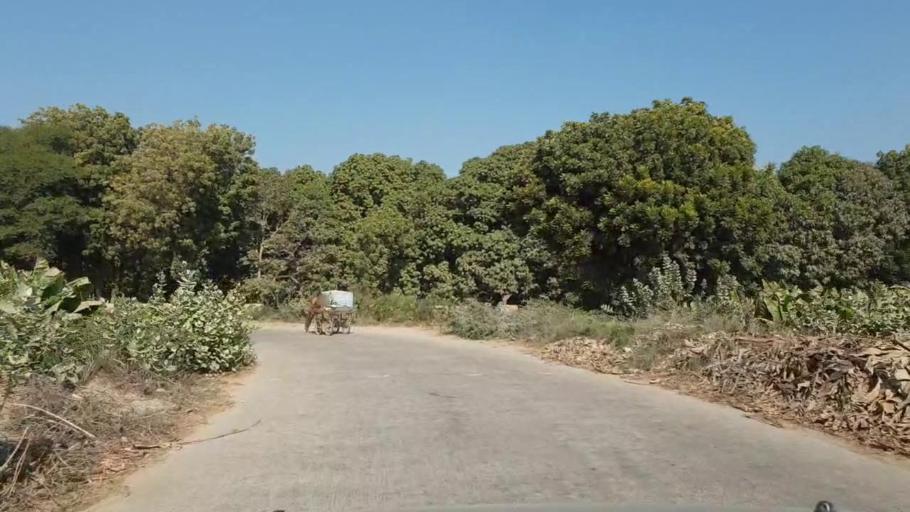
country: PK
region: Sindh
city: Matiari
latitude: 25.6191
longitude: 68.5942
